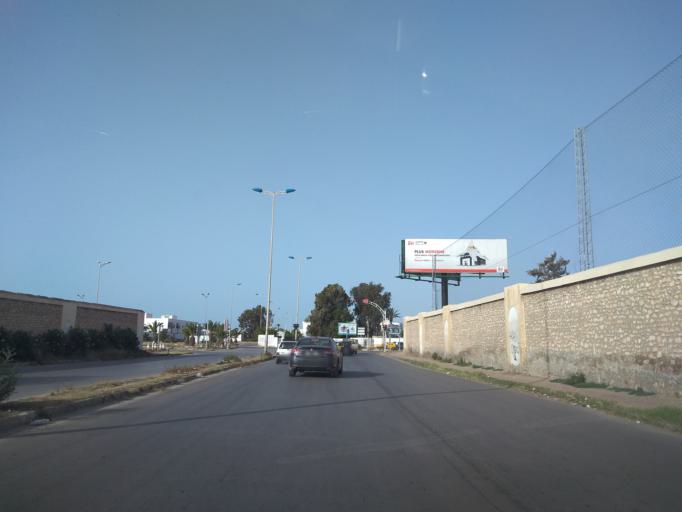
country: TN
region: Safaqis
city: Sfax
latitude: 34.7321
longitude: 10.7467
